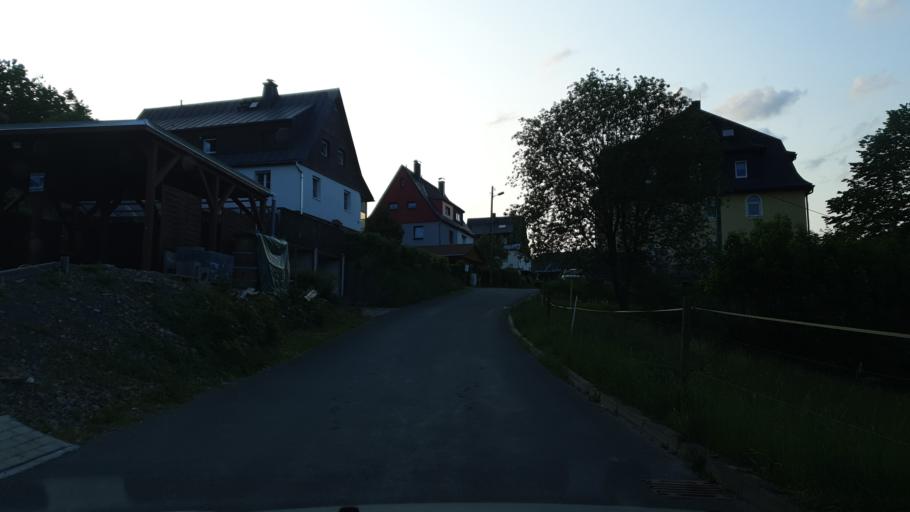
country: DE
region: Saxony
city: Klingenthal
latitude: 50.3785
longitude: 12.4604
